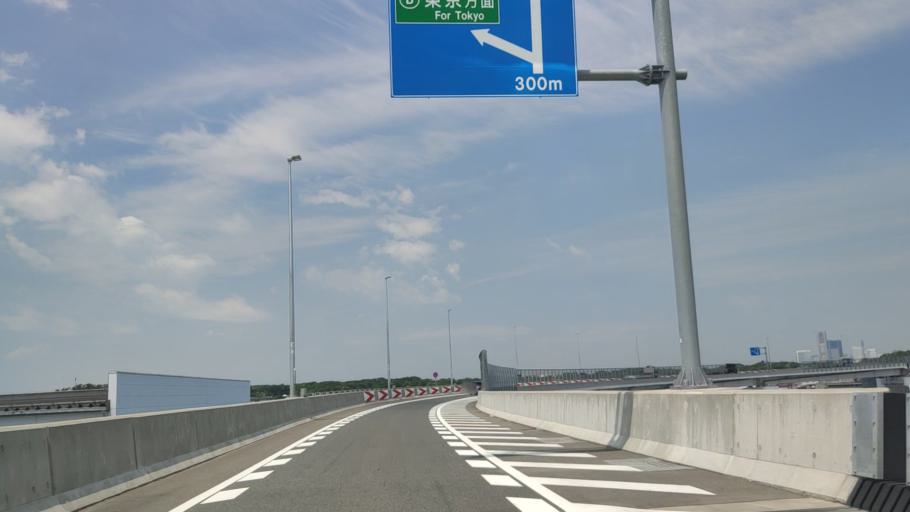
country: JP
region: Kanagawa
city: Yokohama
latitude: 35.4146
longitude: 139.6728
